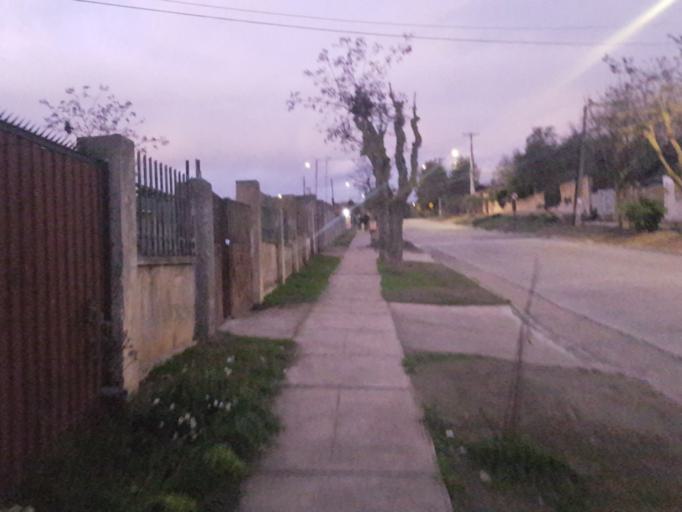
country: CL
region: Valparaiso
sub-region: Provincia de Marga Marga
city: Villa Alemana
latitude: -33.0388
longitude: -71.3497
